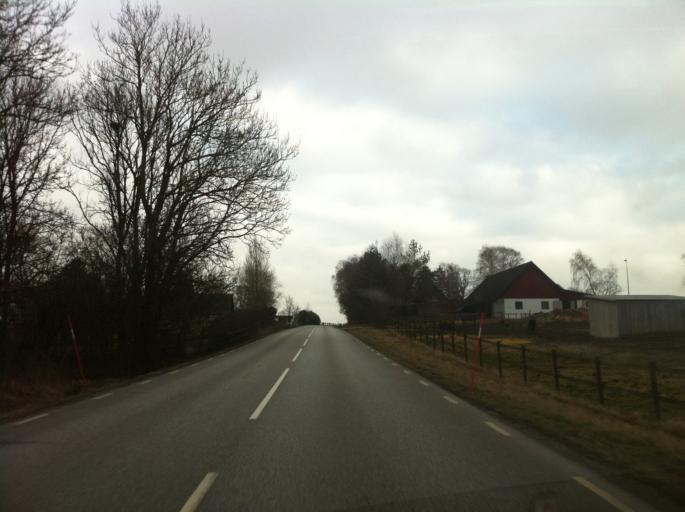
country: SE
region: Skane
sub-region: Kavlinge Kommun
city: Hofterup
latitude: 55.8231
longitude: 12.9924
